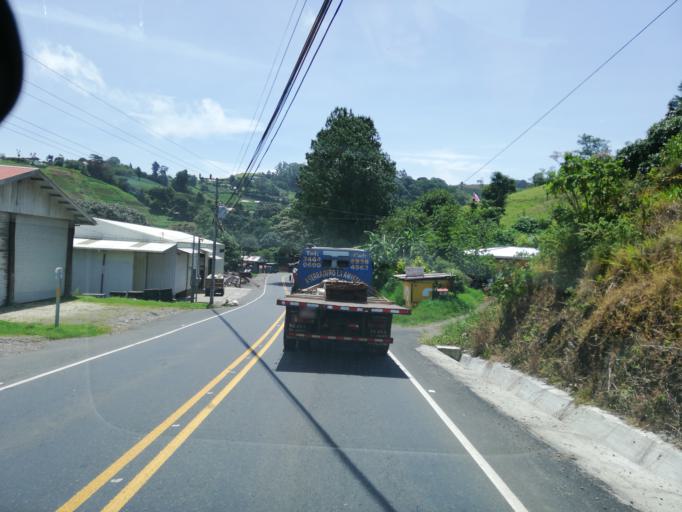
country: CR
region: Alajuela
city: Zarcero
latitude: 10.2141
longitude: -84.3996
